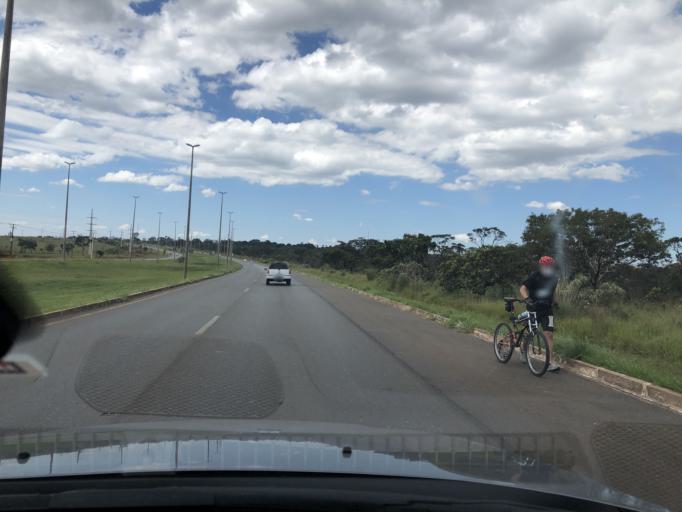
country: BR
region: Federal District
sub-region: Brasilia
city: Brasilia
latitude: -15.9770
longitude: -48.0082
